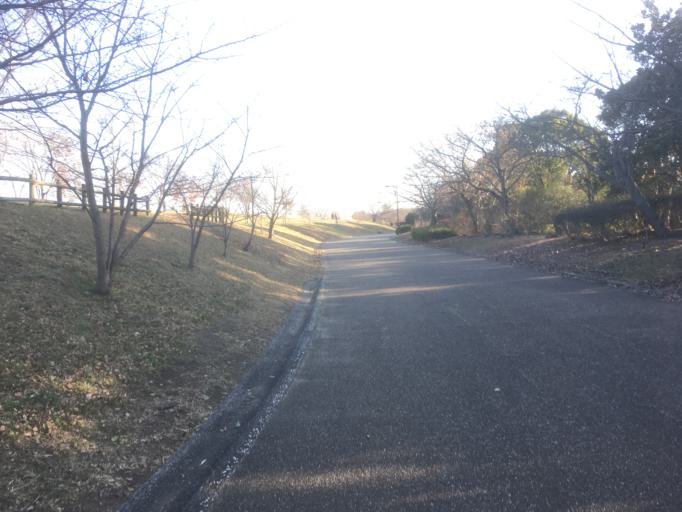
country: JP
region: Nara
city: Tawaramoto
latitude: 34.5686
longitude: 135.7369
